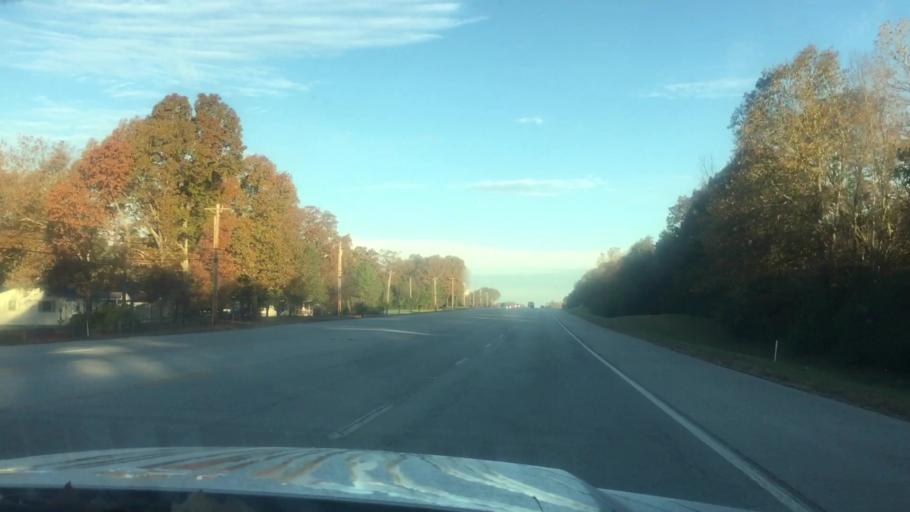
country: US
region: Tennessee
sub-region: Coffee County
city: Tullahoma
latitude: 35.3233
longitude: -86.1746
